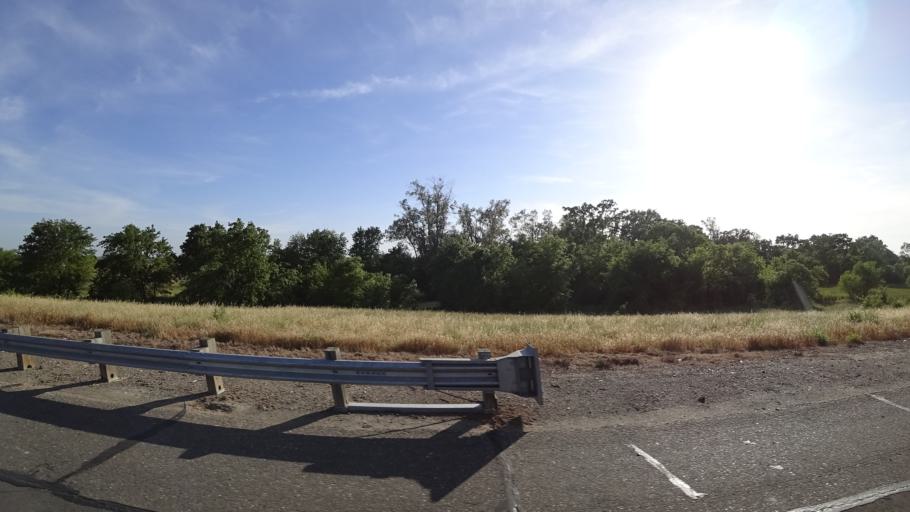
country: US
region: California
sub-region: Yuba County
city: Olivehurst
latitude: 39.0712
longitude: -121.5226
